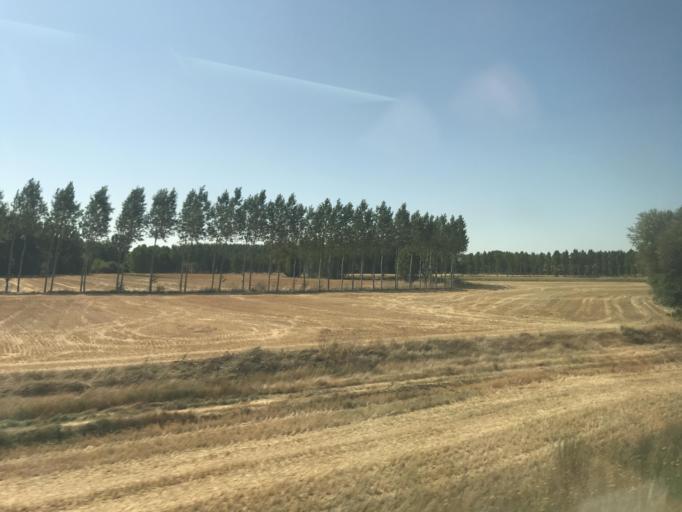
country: ES
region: Castille and Leon
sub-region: Provincia de Burgos
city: Estepar
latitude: 42.2811
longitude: -3.8729
